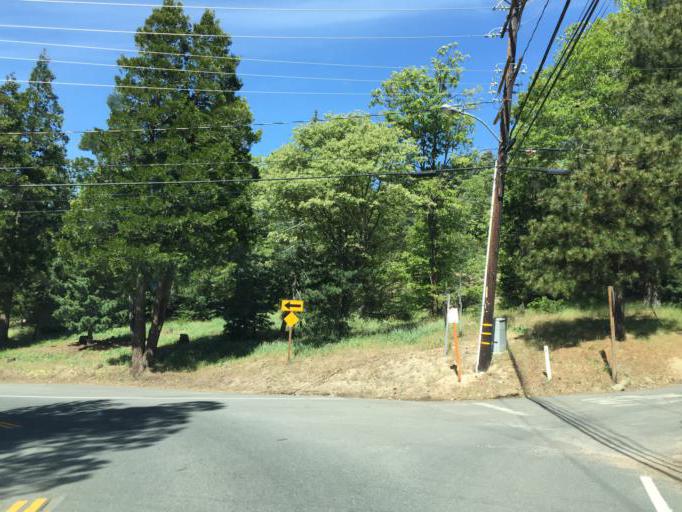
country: US
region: California
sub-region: San Bernardino County
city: Crestline
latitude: 34.2365
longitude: -117.2423
